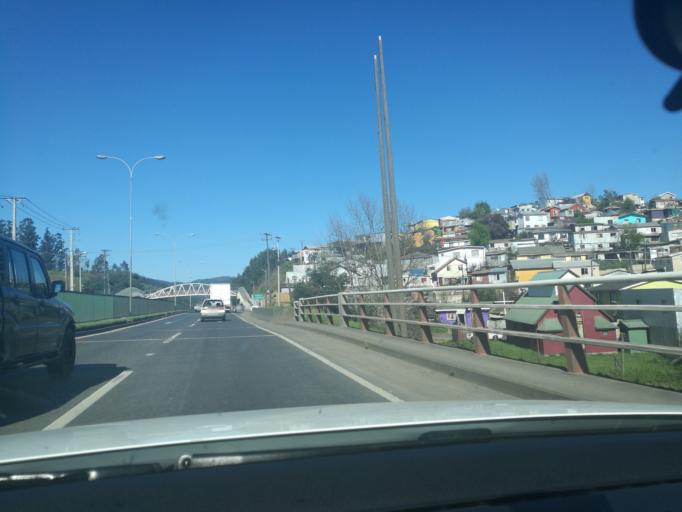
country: CL
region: Biobio
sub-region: Provincia de Concepcion
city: Concepcion
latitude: -36.8062
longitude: -73.0366
